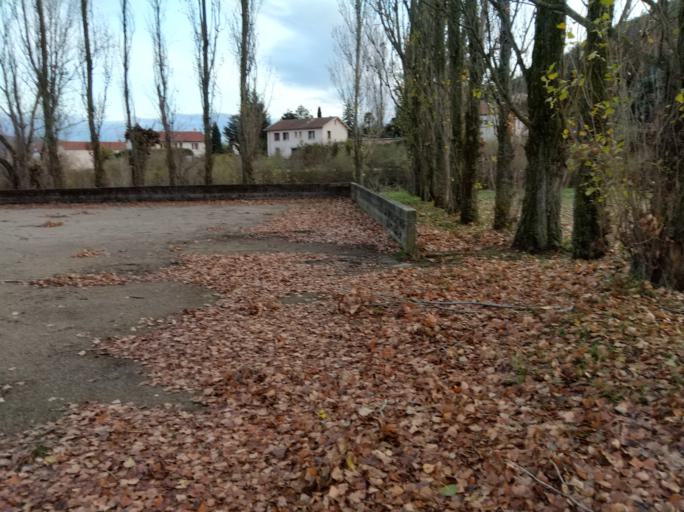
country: FR
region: Rhone-Alpes
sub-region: Departement de l'Ardeche
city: Sarras
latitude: 45.1921
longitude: 4.7942
